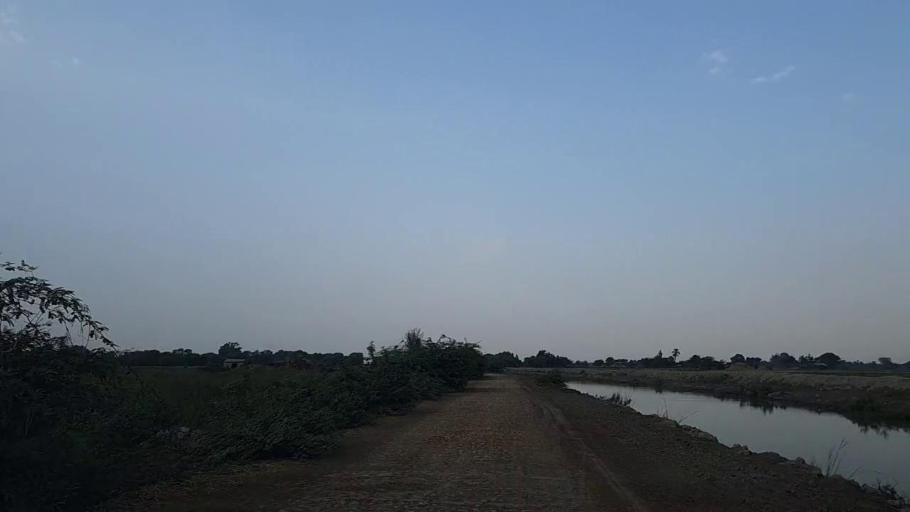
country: PK
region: Sindh
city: Daro Mehar
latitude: 24.7616
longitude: 68.1359
